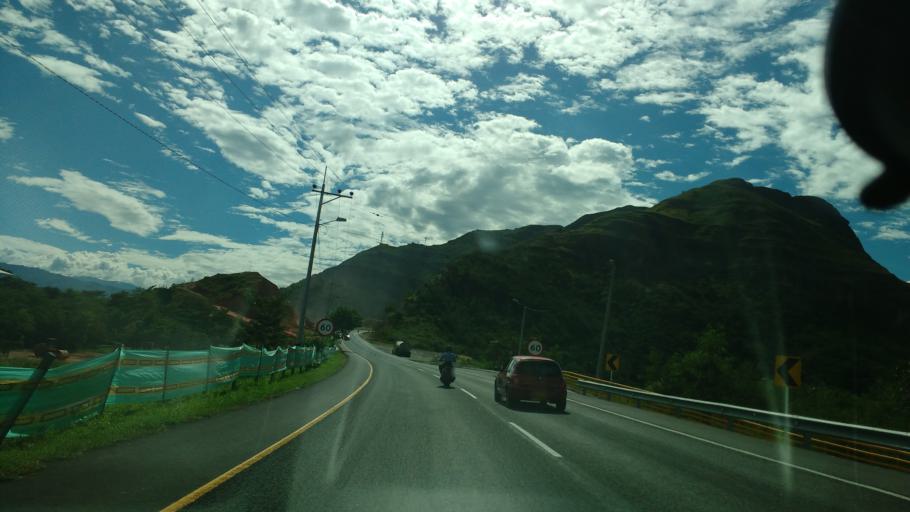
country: CO
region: Tolima
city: Valle de San Juan
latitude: 4.2805
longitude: -75.0155
